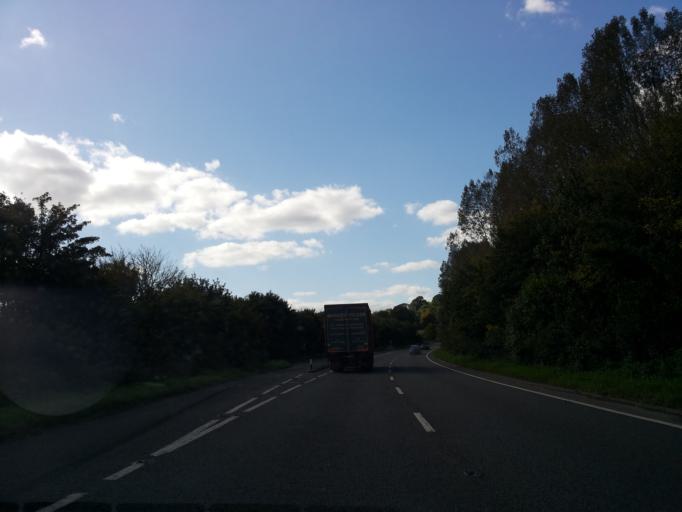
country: GB
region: England
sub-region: Wiltshire
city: Warminster
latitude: 51.1898
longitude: -2.1827
